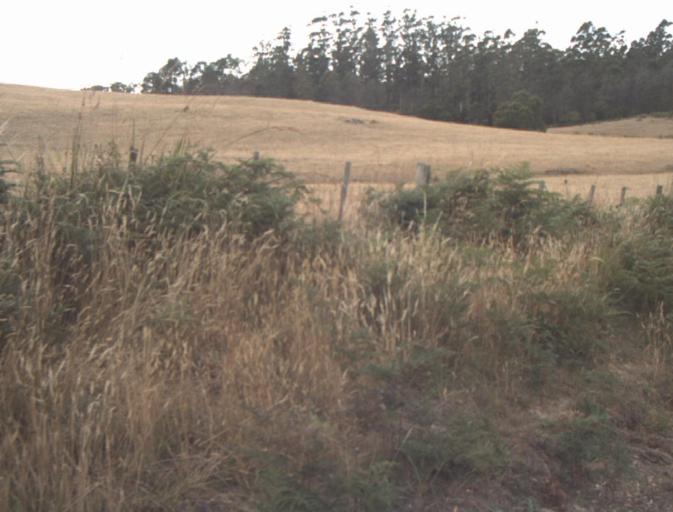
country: AU
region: Tasmania
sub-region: Launceston
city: Mayfield
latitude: -41.1990
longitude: 147.2278
